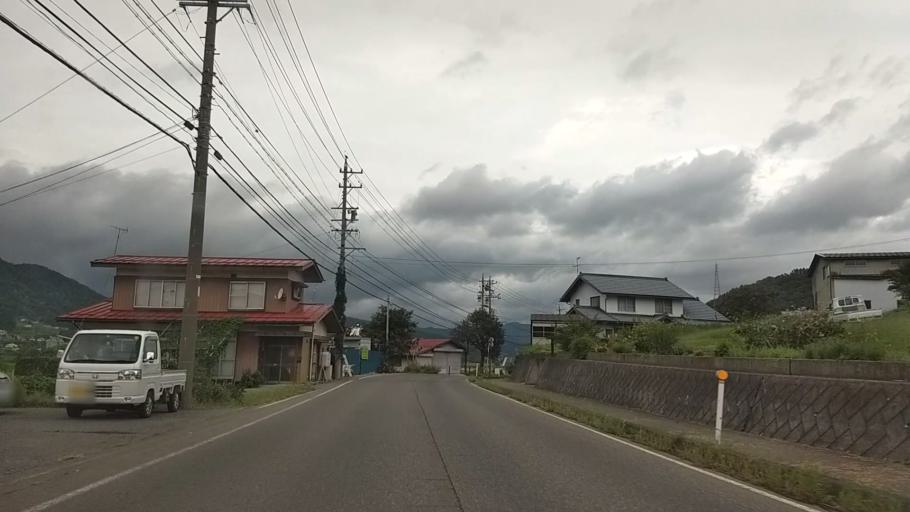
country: JP
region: Nagano
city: Iiyama
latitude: 36.8138
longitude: 138.3600
